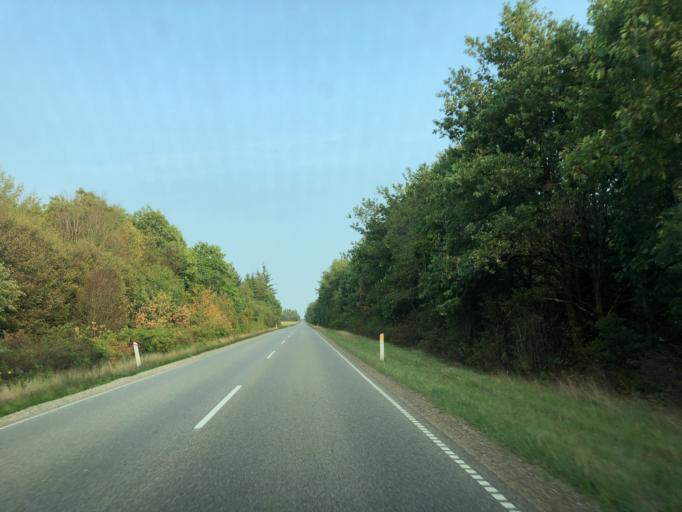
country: DK
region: South Denmark
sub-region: Billund Kommune
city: Grindsted
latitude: 55.8291
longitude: 8.9650
